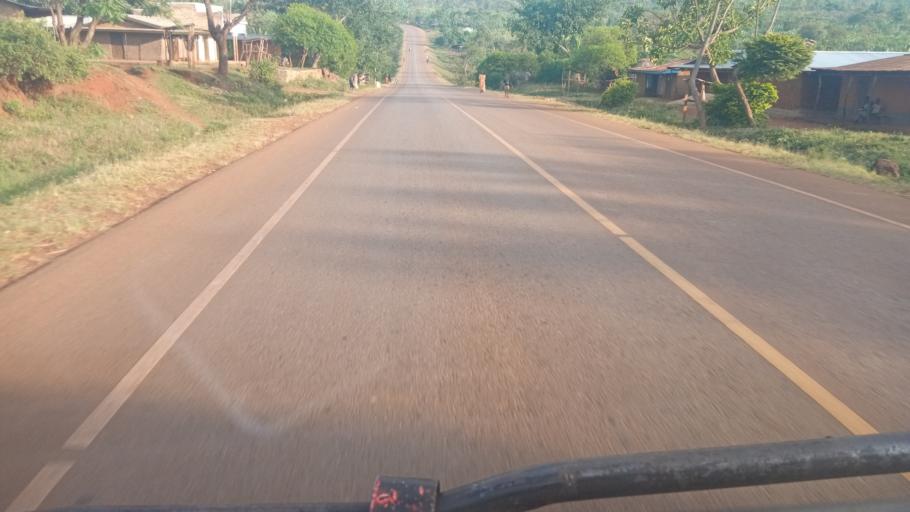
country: UG
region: Eastern Region
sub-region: Sironko District
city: Sironko
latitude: 1.3322
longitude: 34.3233
